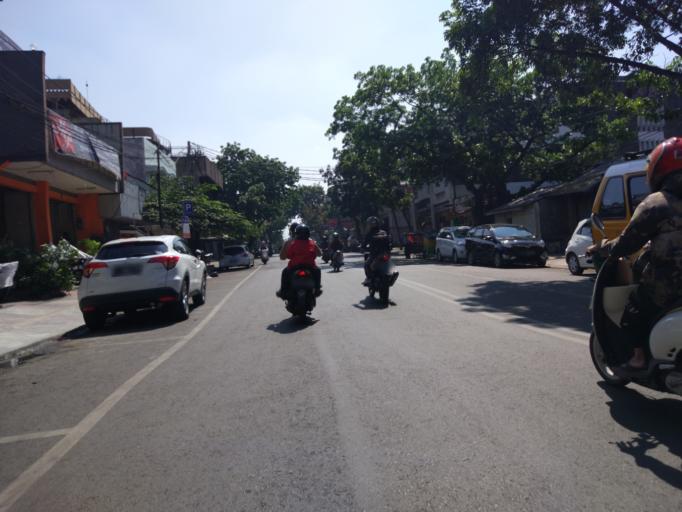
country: ID
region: West Java
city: Bandung
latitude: -6.9341
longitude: 107.5961
